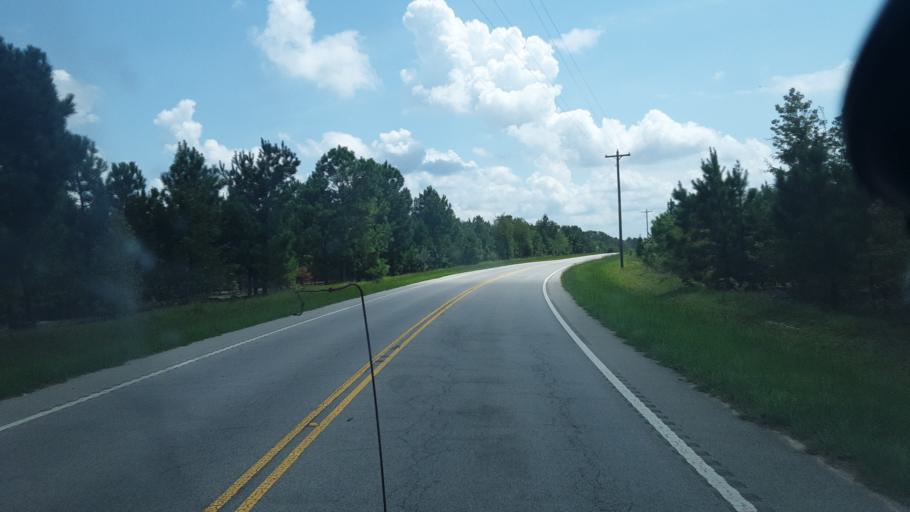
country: US
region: South Carolina
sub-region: Calhoun County
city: Oak Grove
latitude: 33.7038
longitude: -80.9570
